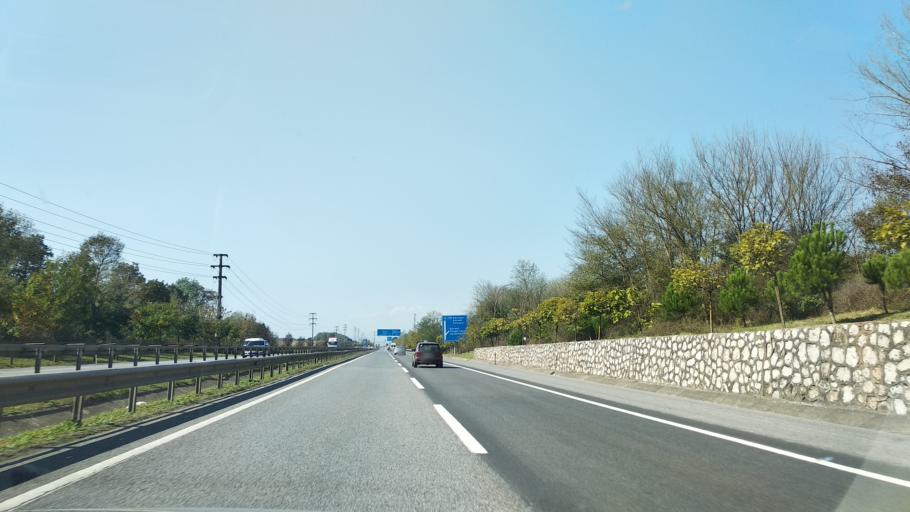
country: TR
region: Kocaeli
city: Derbent
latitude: 40.7420
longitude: 30.0874
